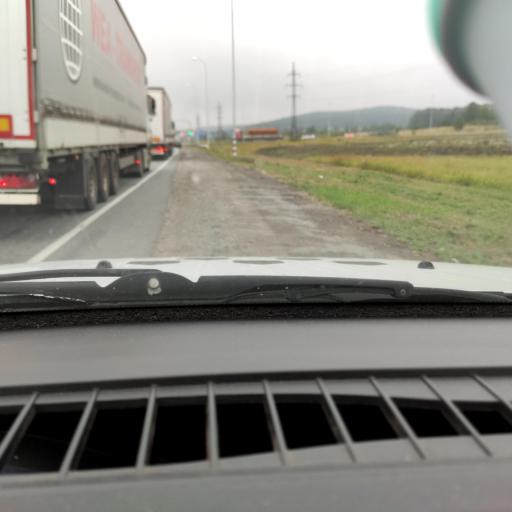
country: RU
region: Chelyabinsk
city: Miass
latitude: 54.9440
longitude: 60.0480
